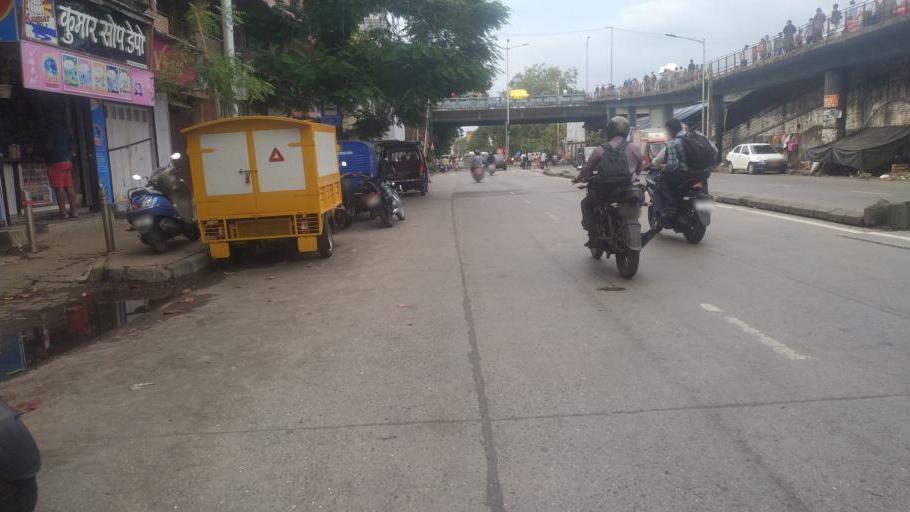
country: IN
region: Maharashtra
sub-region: Mumbai Suburban
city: Mumbai
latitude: 19.0297
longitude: 72.8469
